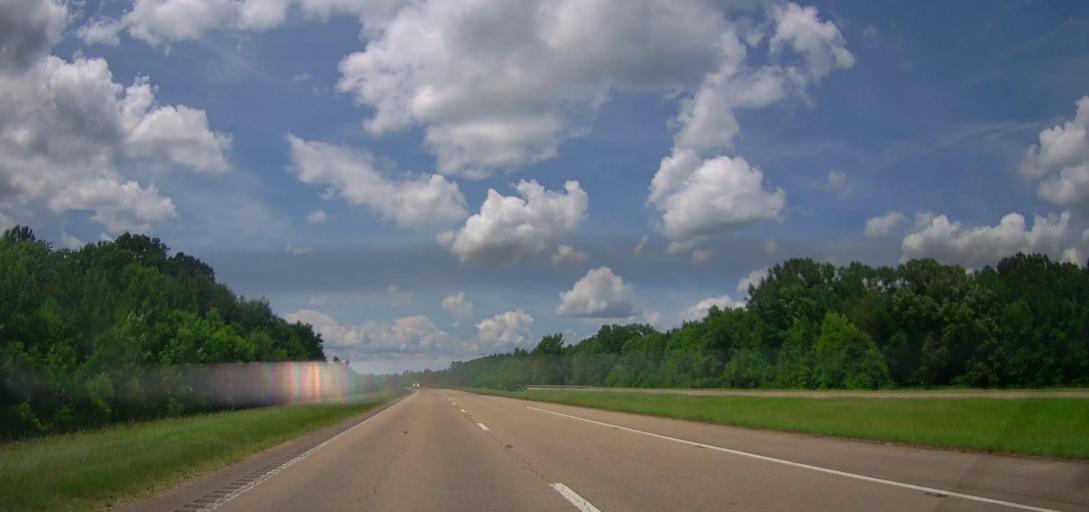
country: US
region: Mississippi
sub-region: Lee County
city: Nettleton
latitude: 34.0882
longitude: -88.6381
